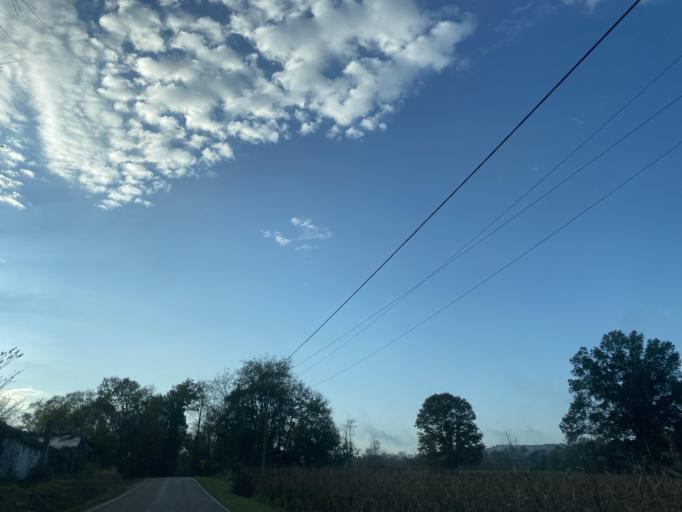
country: US
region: Kentucky
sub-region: Pendleton County
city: Falmouth
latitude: 38.7534
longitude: -84.3391
